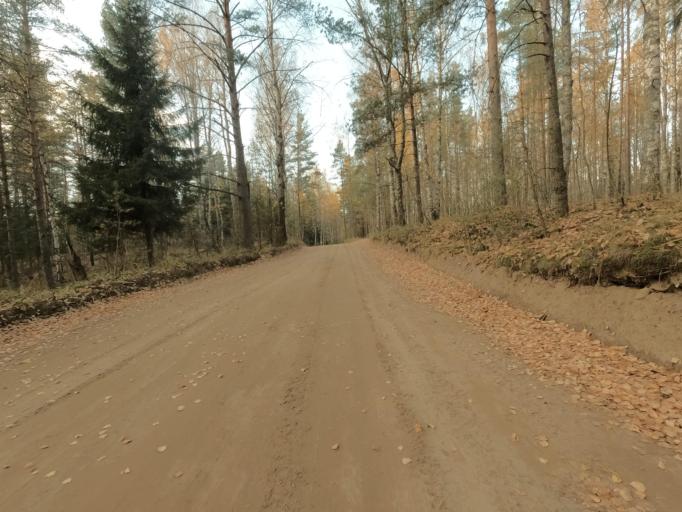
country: RU
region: Leningrad
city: Priladozhskiy
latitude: 59.7405
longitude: 31.3150
